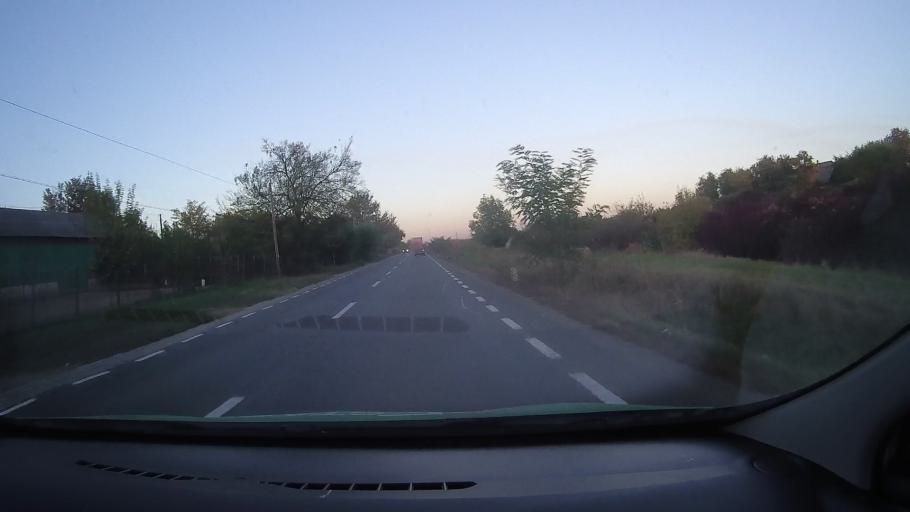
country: RO
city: Szekelyhid
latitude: 47.3627
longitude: 22.1161
